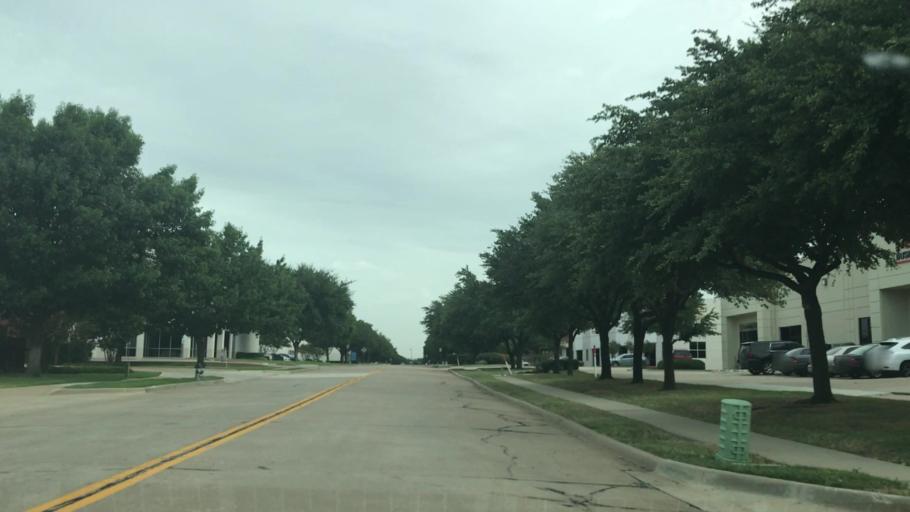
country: US
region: Texas
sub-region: Dallas County
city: Coppell
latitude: 32.9168
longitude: -97.0027
